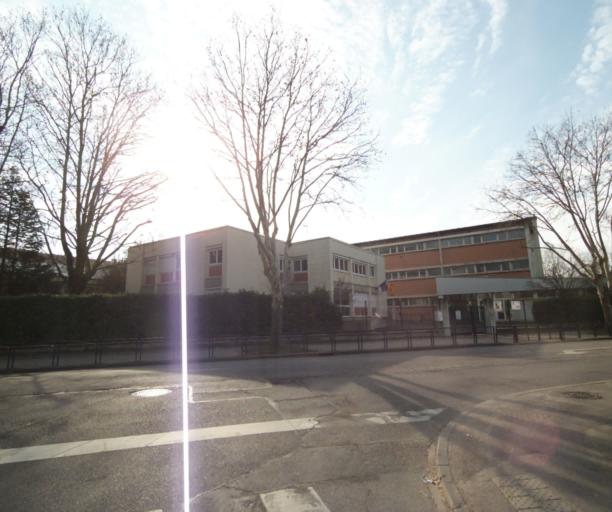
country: FR
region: Lorraine
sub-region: Departement de Meurthe-et-Moselle
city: Villers-les-Nancy
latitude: 48.6709
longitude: 6.1592
